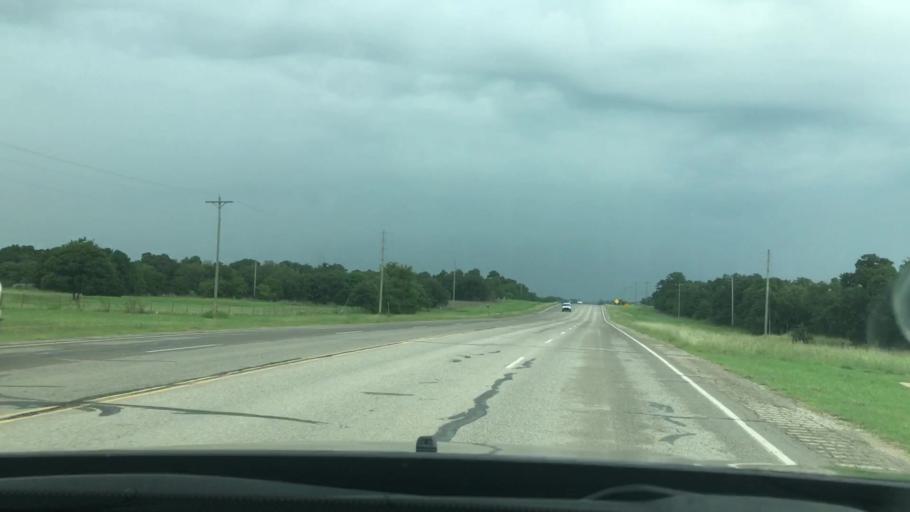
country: US
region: Oklahoma
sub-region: Carter County
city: Healdton
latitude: 34.1930
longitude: -97.4747
